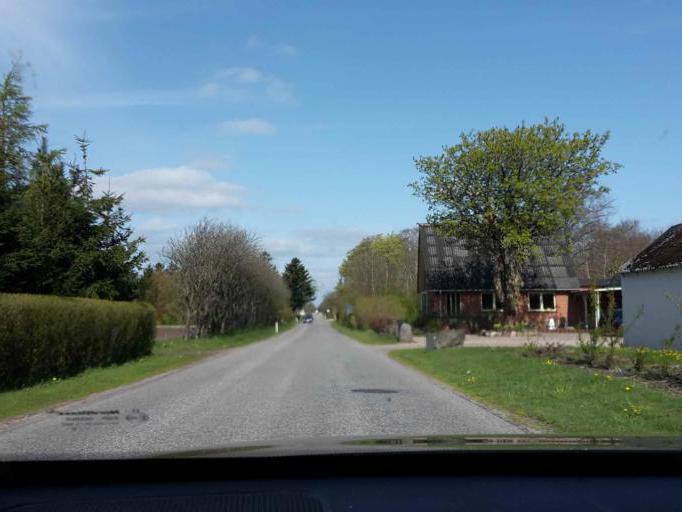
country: DK
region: South Denmark
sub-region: Vejen Kommune
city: Brorup
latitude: 55.5681
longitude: 9.0106
